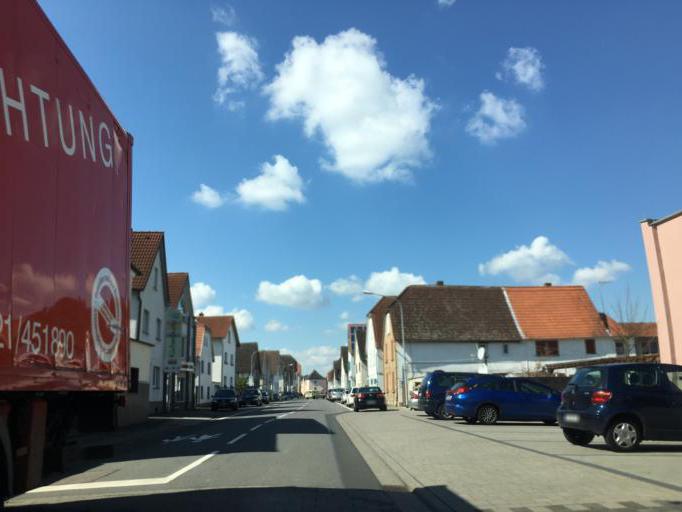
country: DE
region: Hesse
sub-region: Regierungsbezirk Darmstadt
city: Rodgau
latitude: 49.9953
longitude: 8.8712
